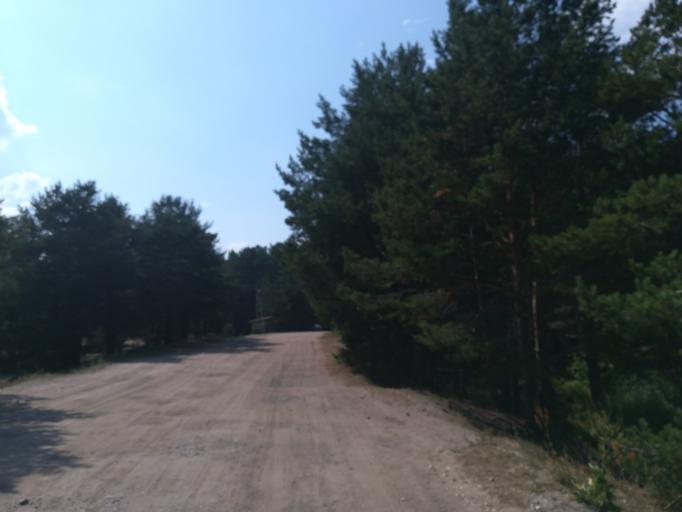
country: RU
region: Leningrad
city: Ust'-Luga
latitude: 59.7743
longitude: 28.1304
